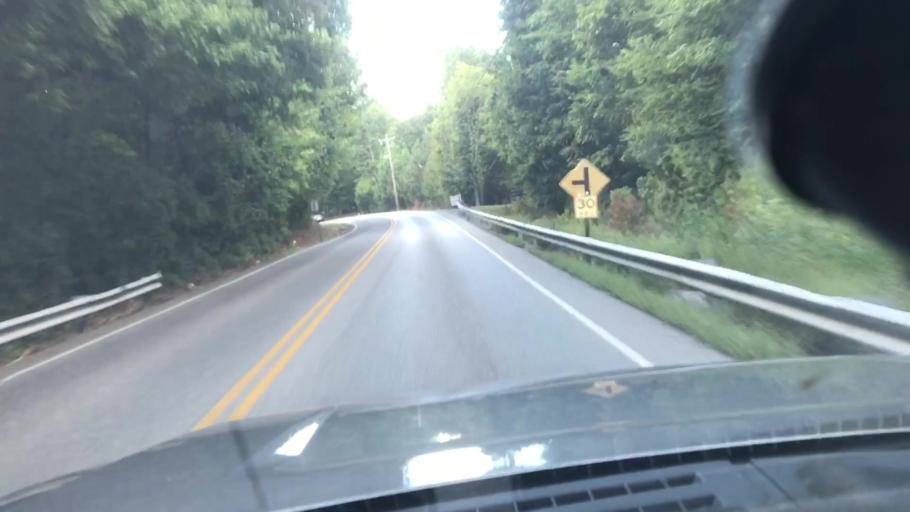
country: US
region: Tennessee
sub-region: Davidson County
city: Forest Hills
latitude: 36.0284
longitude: -86.9382
